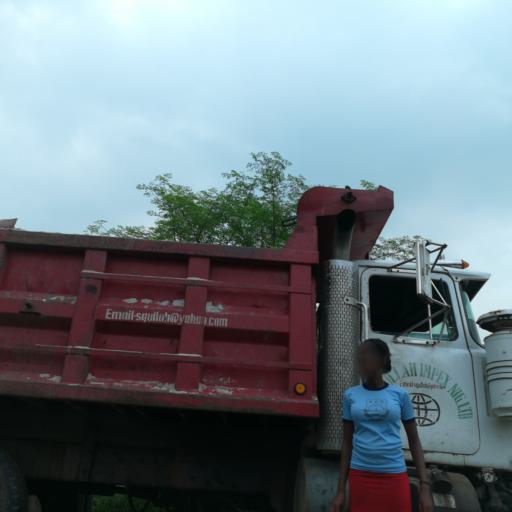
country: NG
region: Rivers
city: Port Harcourt
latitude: 4.8070
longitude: 7.0490
